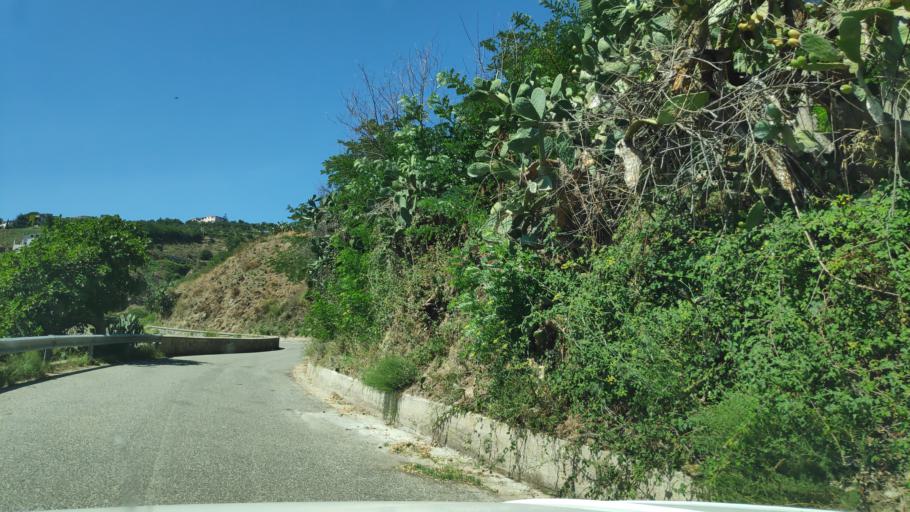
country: IT
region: Calabria
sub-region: Provincia di Catanzaro
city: Montauro
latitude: 38.7464
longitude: 16.5116
